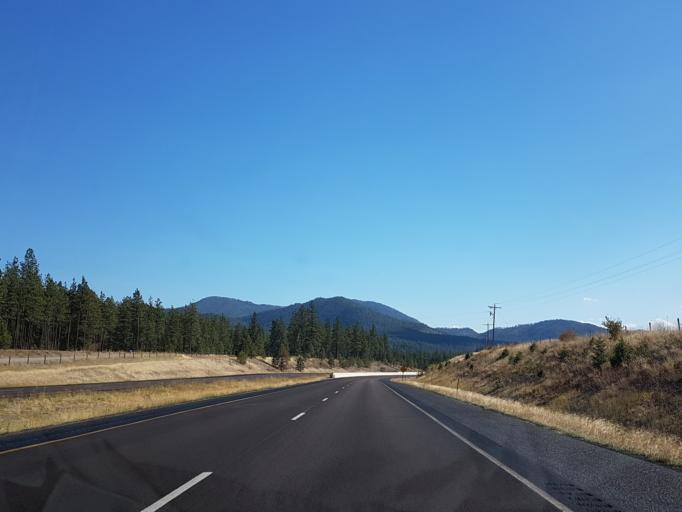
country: US
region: Montana
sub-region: Mineral County
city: Superior
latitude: 47.1354
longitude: -114.8013
